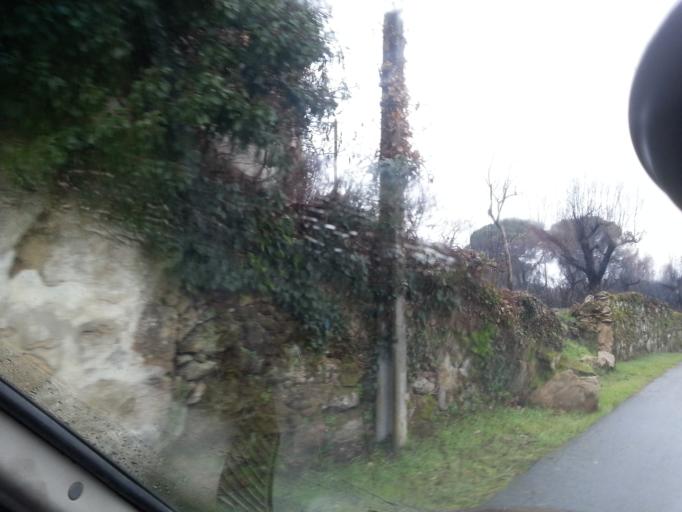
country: PT
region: Viseu
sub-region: Mangualde
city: Mangualde
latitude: 40.6145
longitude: -7.7822
